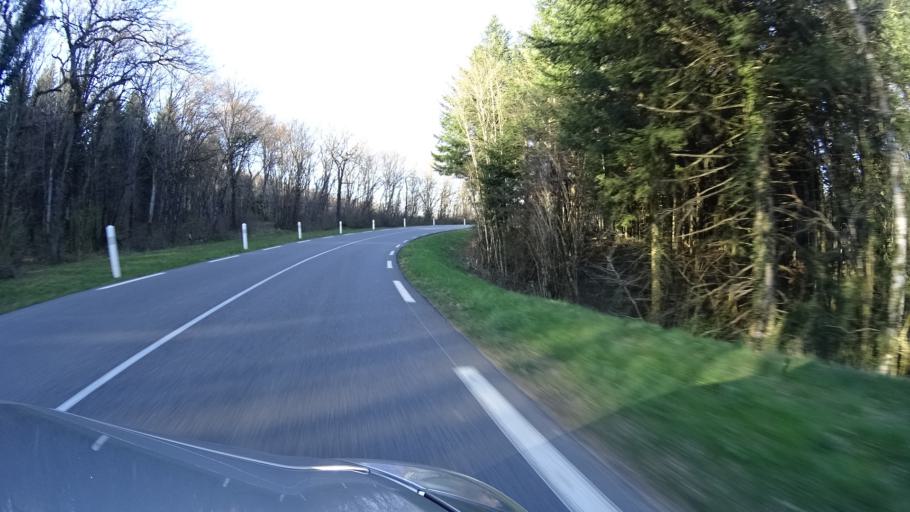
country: FR
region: Franche-Comte
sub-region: Departement du Doubs
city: Beure
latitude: 47.1848
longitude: 6.0085
